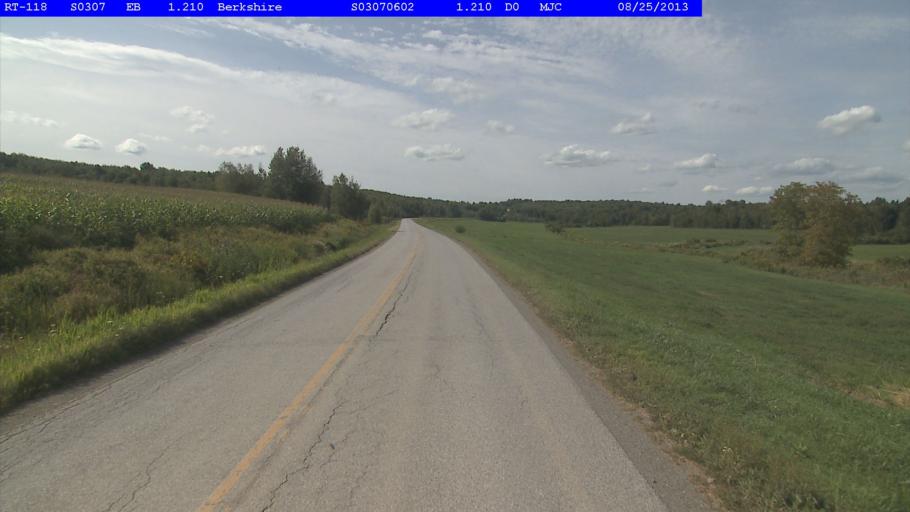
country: US
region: Vermont
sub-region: Franklin County
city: Enosburg Falls
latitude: 44.9391
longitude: -72.7339
